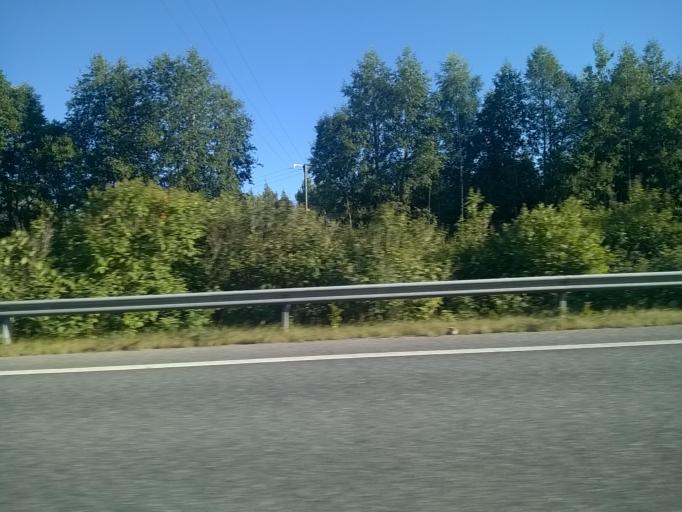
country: FI
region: Pirkanmaa
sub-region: Tampere
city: Tampere
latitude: 61.4702
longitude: 23.8561
